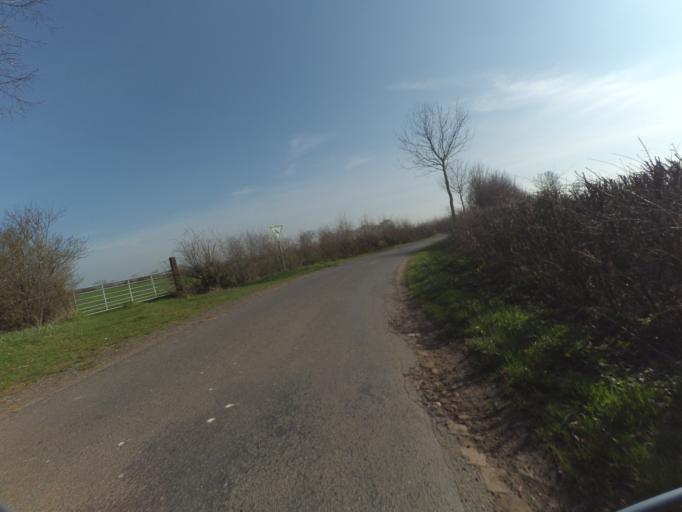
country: DE
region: North Rhine-Westphalia
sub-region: Regierungsbezirk Dusseldorf
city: Kranenburg
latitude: 51.8203
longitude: 5.9895
